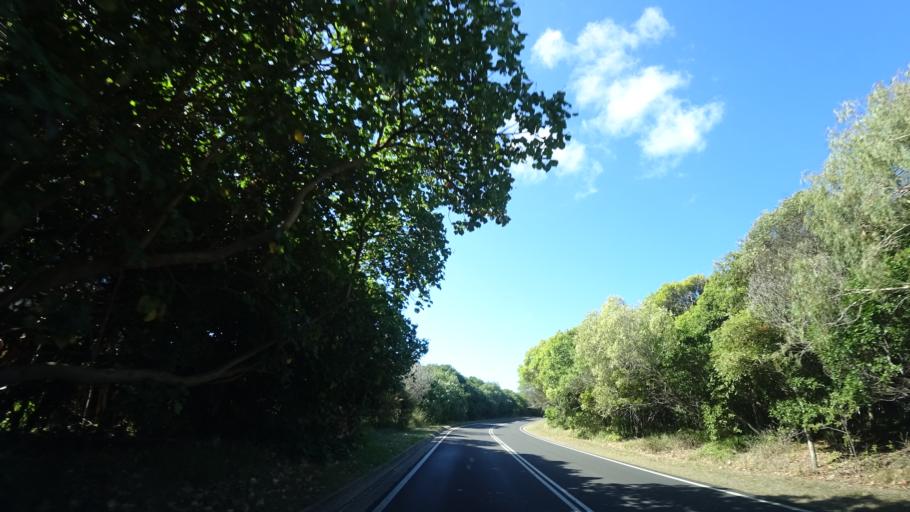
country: AU
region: Queensland
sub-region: Sunshine Coast
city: Mooloolaba
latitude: -26.6351
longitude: 153.1005
